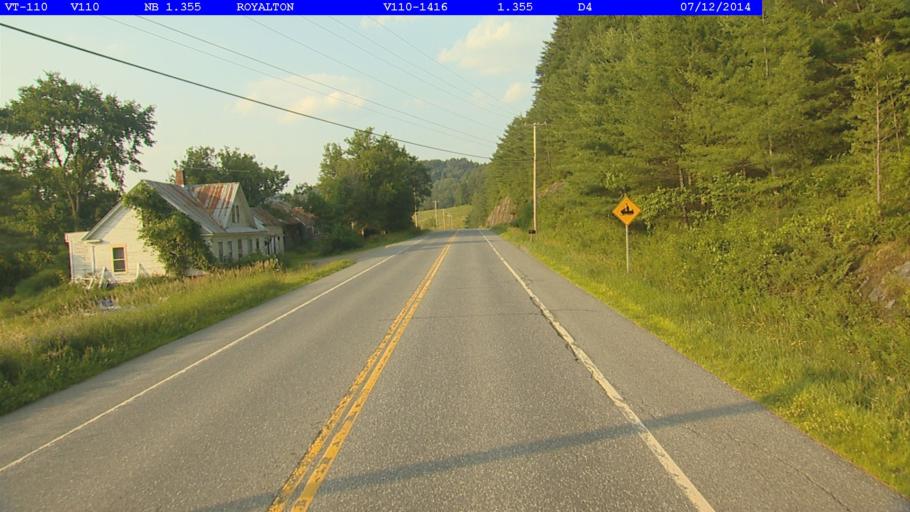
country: US
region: Vermont
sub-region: Orange County
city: Chelsea
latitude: 43.8405
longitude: -72.5136
